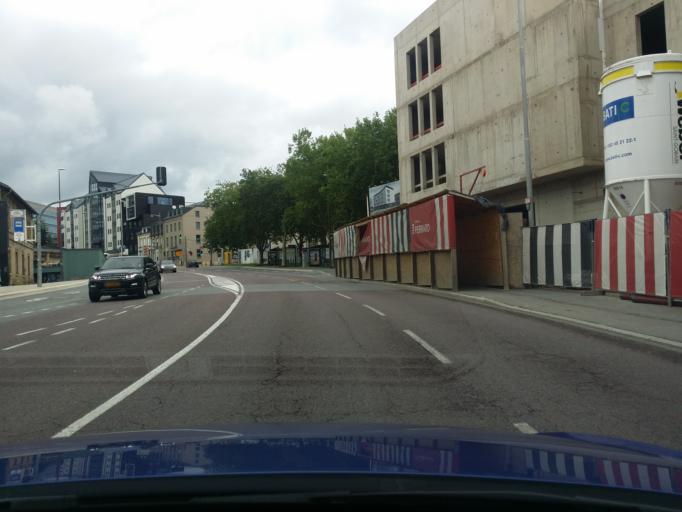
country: LU
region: Luxembourg
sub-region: Canton de Luxembourg
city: Luxembourg
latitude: 49.6007
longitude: 6.1369
